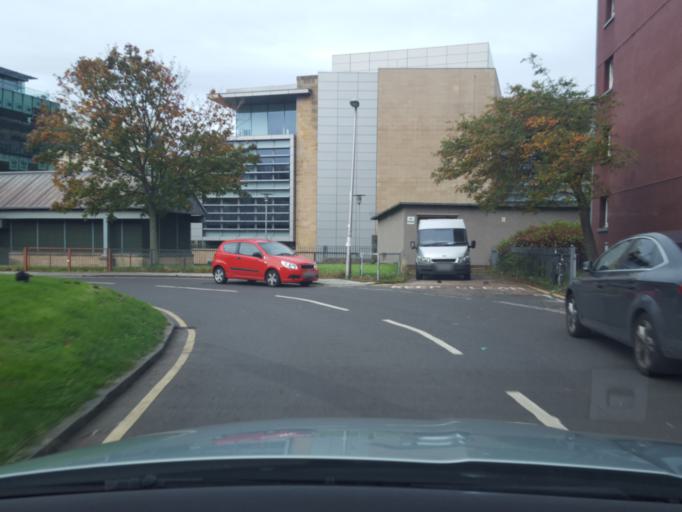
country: GB
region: Scotland
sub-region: Edinburgh
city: Edinburgh
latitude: 55.9497
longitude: -3.1777
